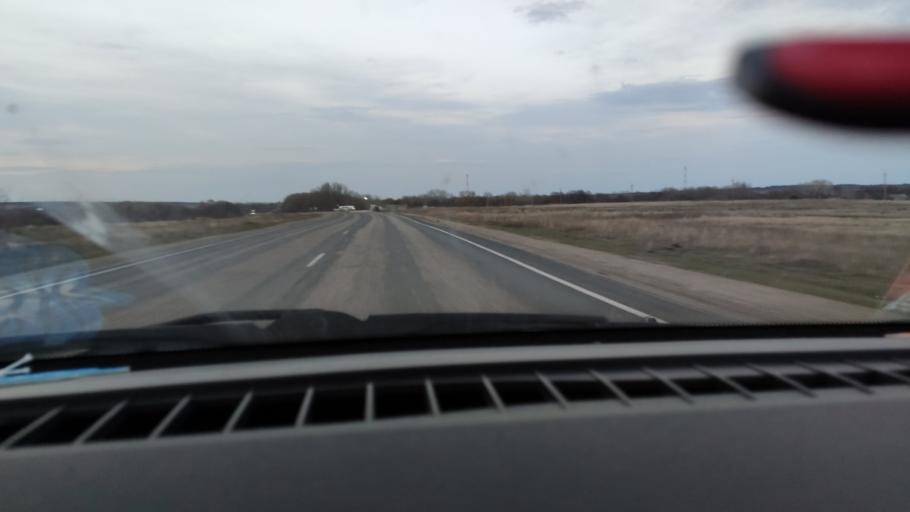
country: RU
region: Saratov
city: Sinodskoye
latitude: 51.9752
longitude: 46.6468
